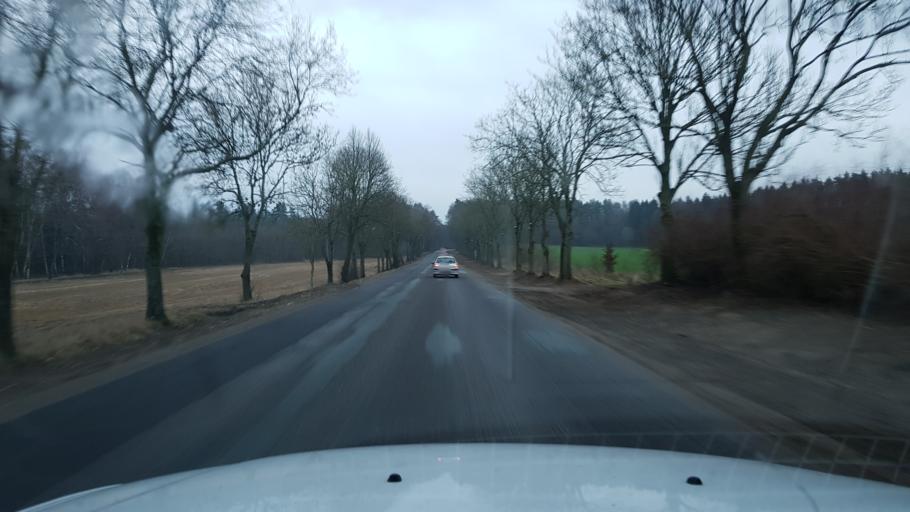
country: PL
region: West Pomeranian Voivodeship
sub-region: Powiat gryficki
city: Gryfice
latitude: 53.8628
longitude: 15.2221
